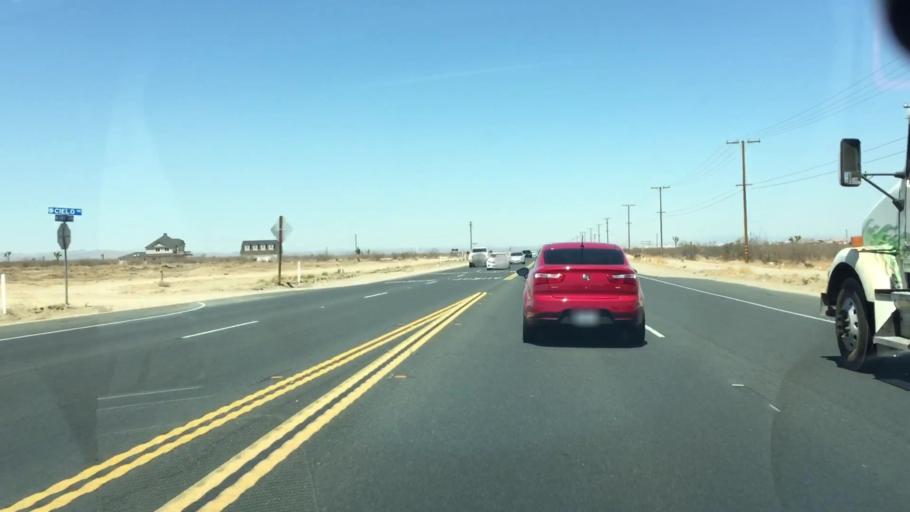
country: US
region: California
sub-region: San Bernardino County
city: Mountain View Acres
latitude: 34.4583
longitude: -117.3996
